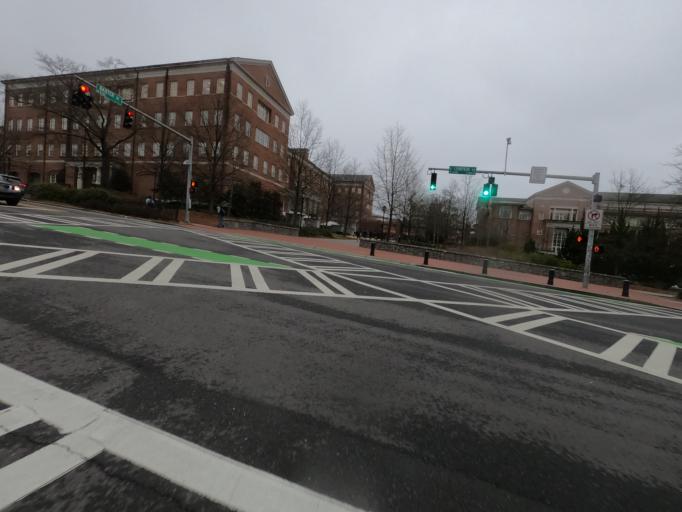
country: US
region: Georgia
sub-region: Clarke County
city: Athens
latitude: 33.9513
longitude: -83.3771
